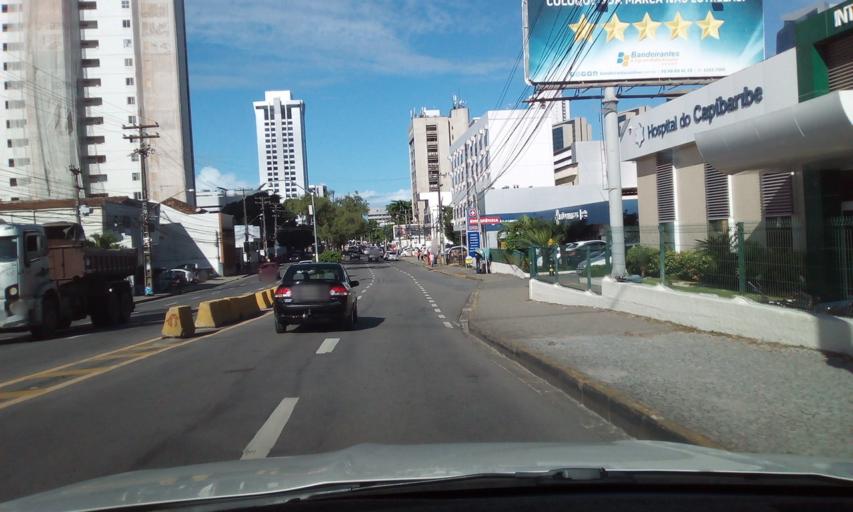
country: BR
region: Pernambuco
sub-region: Recife
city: Recife
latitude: -8.0620
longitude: -34.9002
